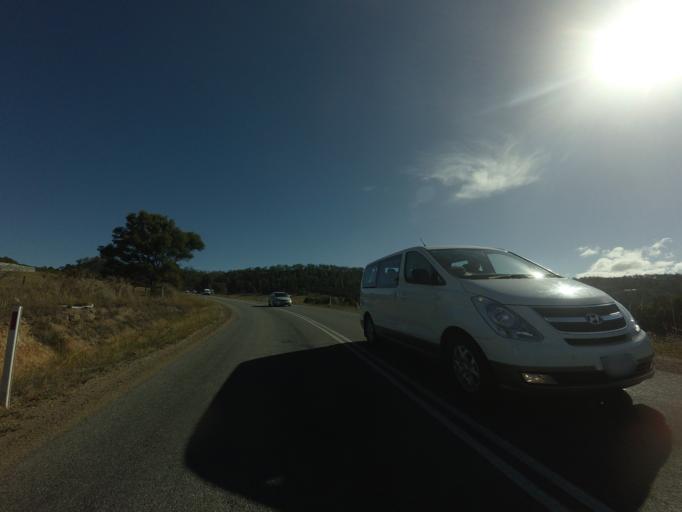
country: AU
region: Tasmania
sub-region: Break O'Day
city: St Helens
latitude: -41.9635
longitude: 148.1538
